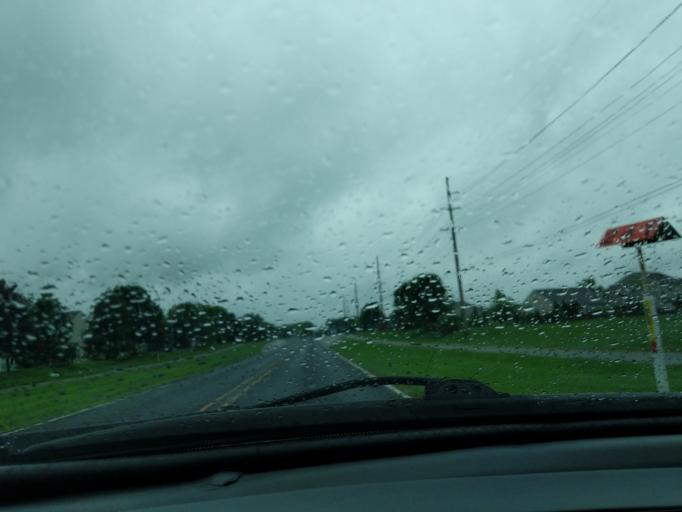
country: US
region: Indiana
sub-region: Hamilton County
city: Noblesville
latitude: 40.0641
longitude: -86.0335
